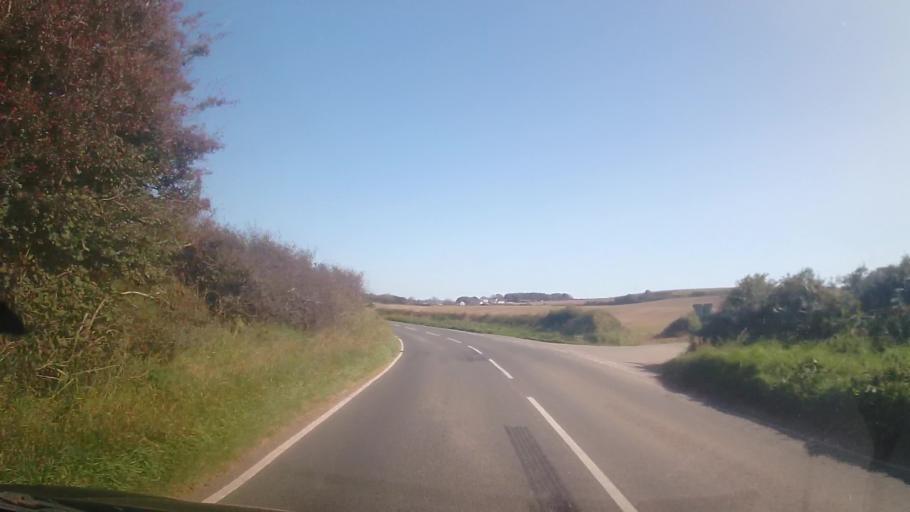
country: GB
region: Wales
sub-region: Pembrokeshire
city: Mathry
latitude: 51.9432
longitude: -5.0659
